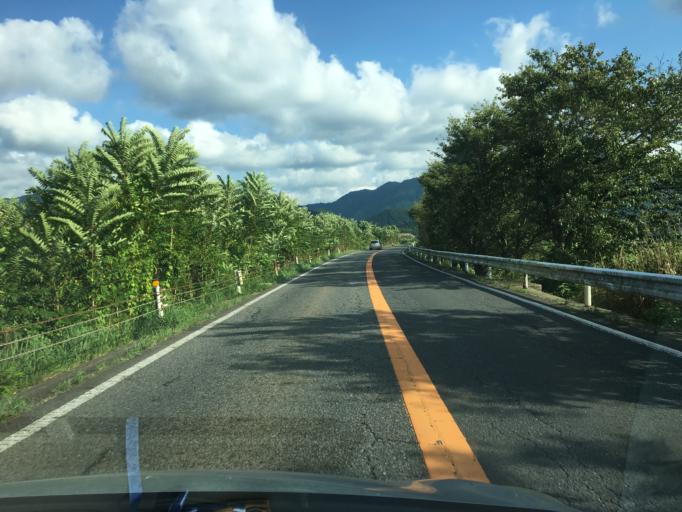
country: JP
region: Hyogo
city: Toyooka
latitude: 35.4393
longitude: 134.7873
